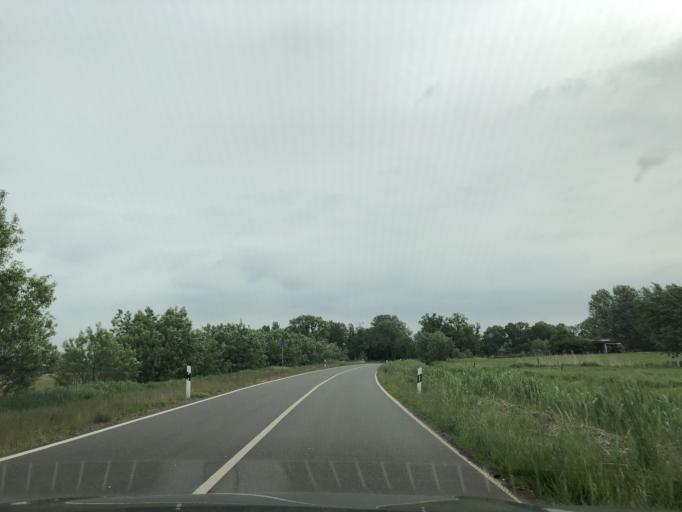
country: DE
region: Brandenburg
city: Plattenburg
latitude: 52.9522
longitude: 12.1335
